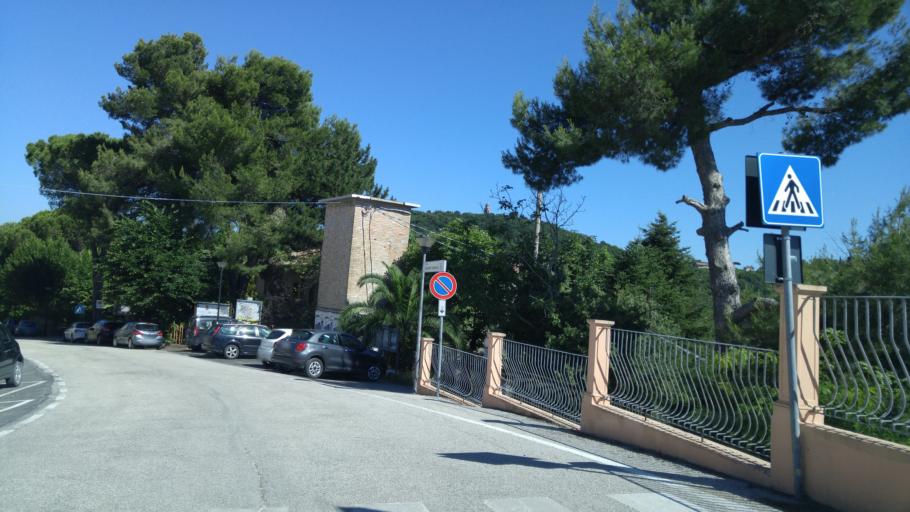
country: IT
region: The Marches
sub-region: Provincia di Pesaro e Urbino
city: Mombaroccio
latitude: 43.7954
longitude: 12.8542
